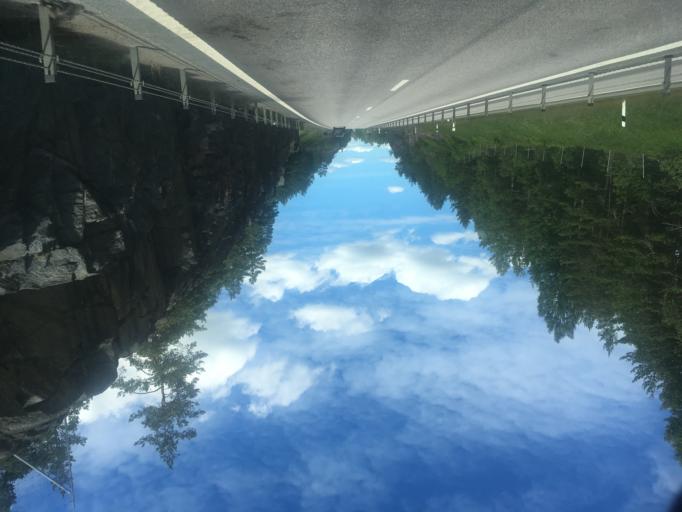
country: SE
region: OEstergoetland
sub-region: Valdemarsviks Kommun
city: Gusum
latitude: 58.3416
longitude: 16.4504
